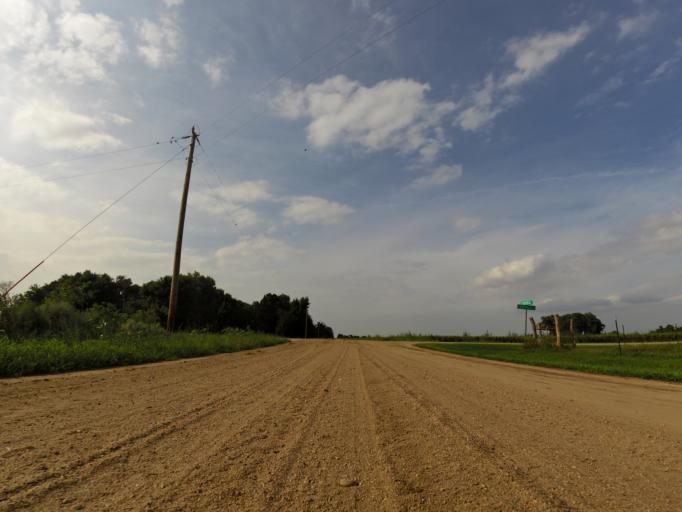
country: US
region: Kansas
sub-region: Reno County
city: South Hutchinson
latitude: 37.9410
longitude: -98.0684
